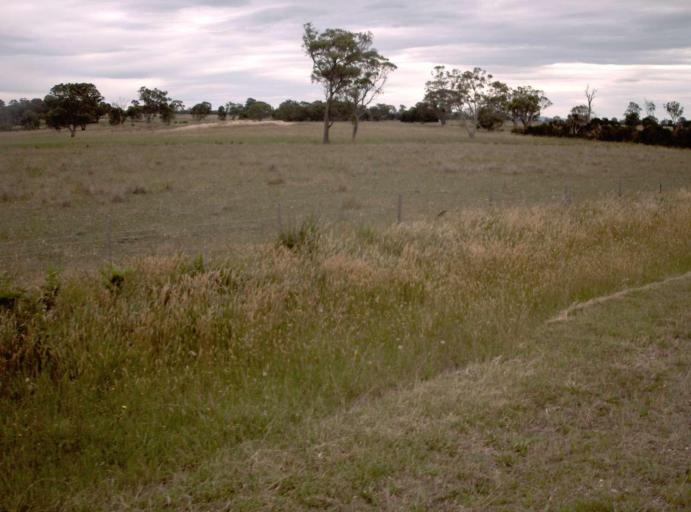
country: AU
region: Victoria
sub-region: East Gippsland
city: Bairnsdale
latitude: -37.9443
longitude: 147.5280
